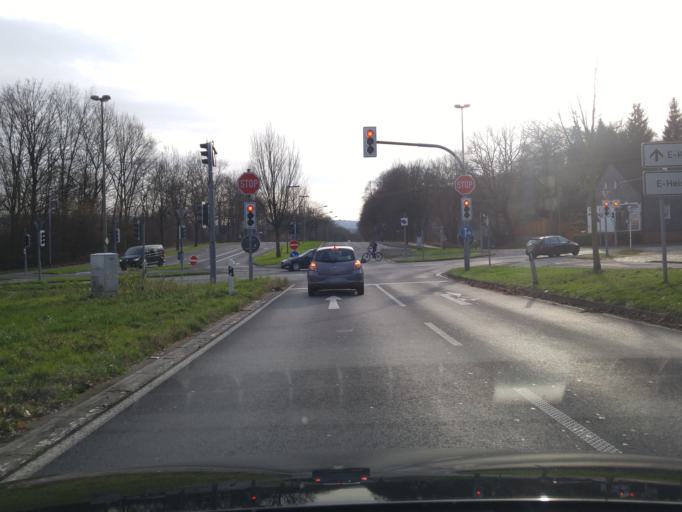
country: DE
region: North Rhine-Westphalia
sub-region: Regierungsbezirk Dusseldorf
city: Essen
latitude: 51.4082
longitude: 7.0737
